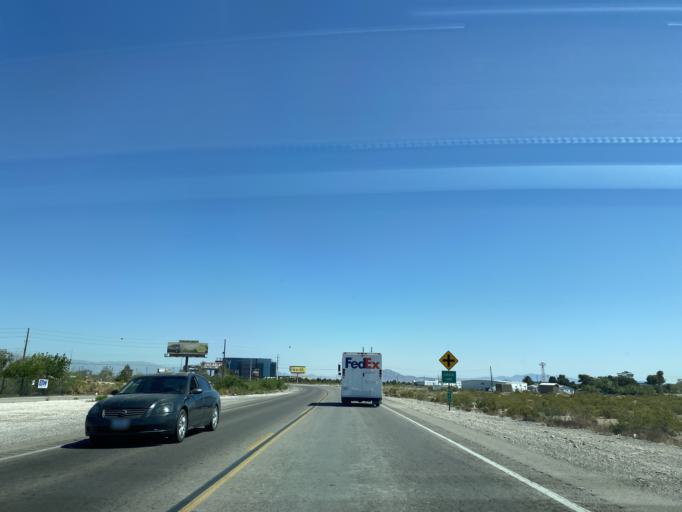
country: US
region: Nevada
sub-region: Clark County
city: Enterprise
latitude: 35.9533
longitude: -115.1748
